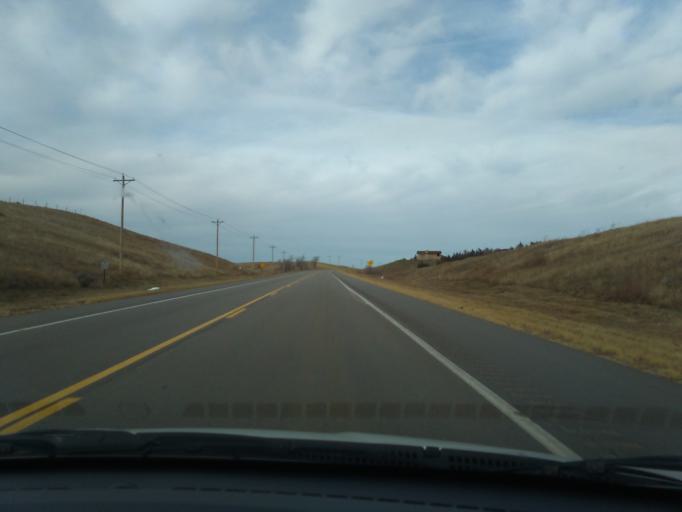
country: US
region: Nebraska
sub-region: Dundy County
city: Benkelman
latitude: 40.0475
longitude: -101.5437
